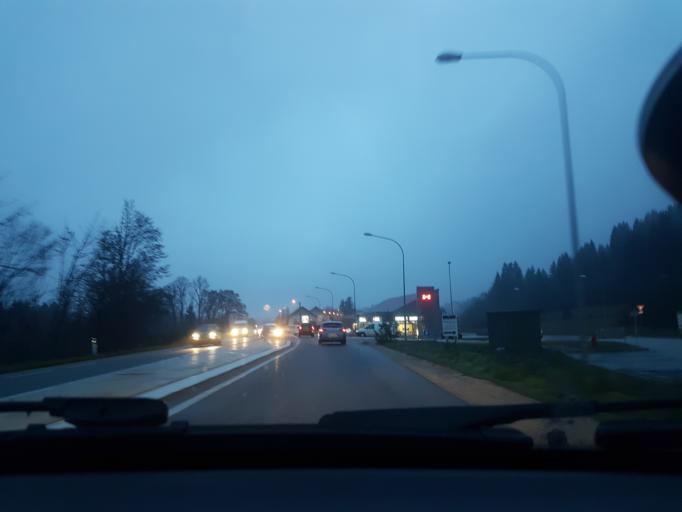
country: FR
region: Franche-Comte
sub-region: Departement du Doubs
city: La Cluse-et-Mijoux
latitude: 46.8875
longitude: 6.3653
